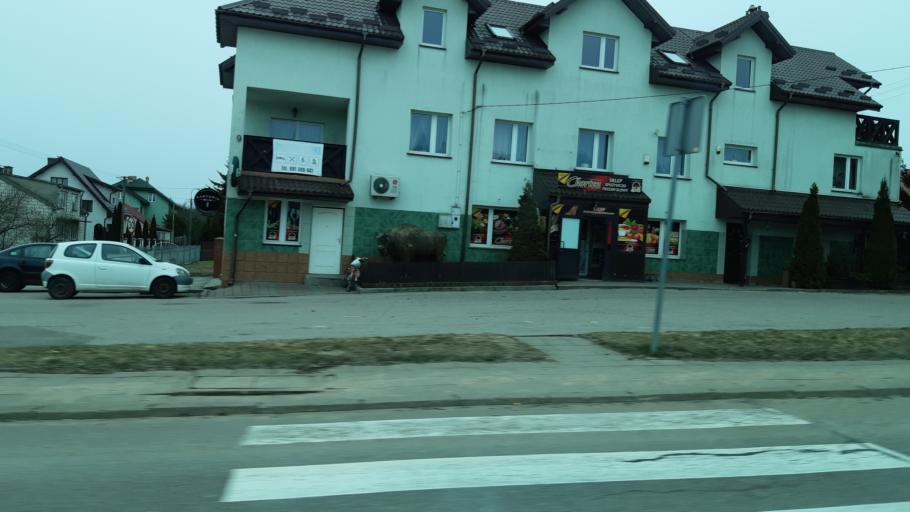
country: PL
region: Podlasie
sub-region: Suwalki
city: Suwalki
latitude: 54.3261
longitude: 22.9671
